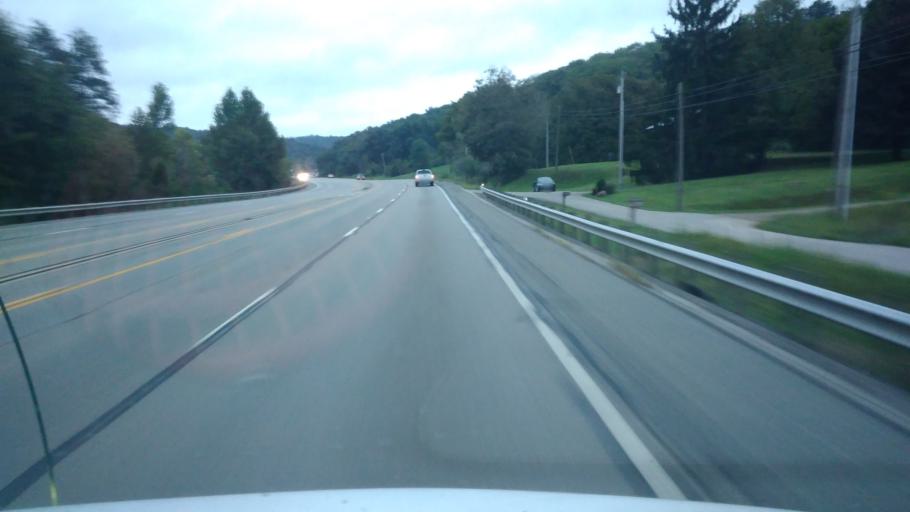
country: US
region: Ohio
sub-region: Ross County
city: Chillicothe
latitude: 39.2329
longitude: -82.9845
